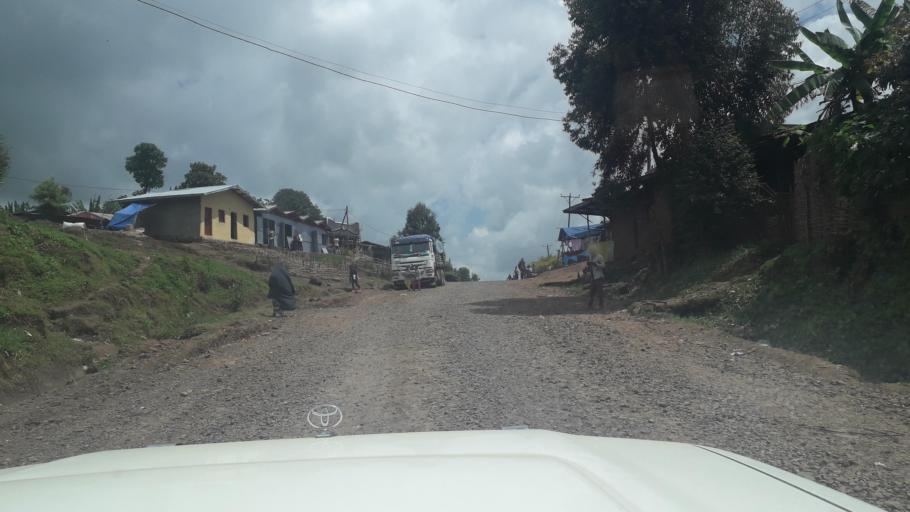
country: ET
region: Oromiya
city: Jima
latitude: 7.4207
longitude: 36.8713
